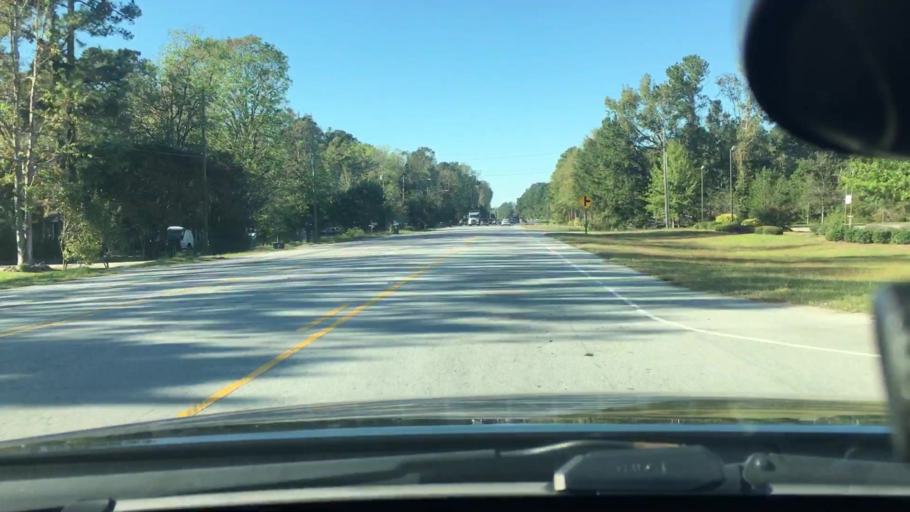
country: US
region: North Carolina
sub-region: Craven County
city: Trent Woods
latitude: 35.1474
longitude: -77.1072
